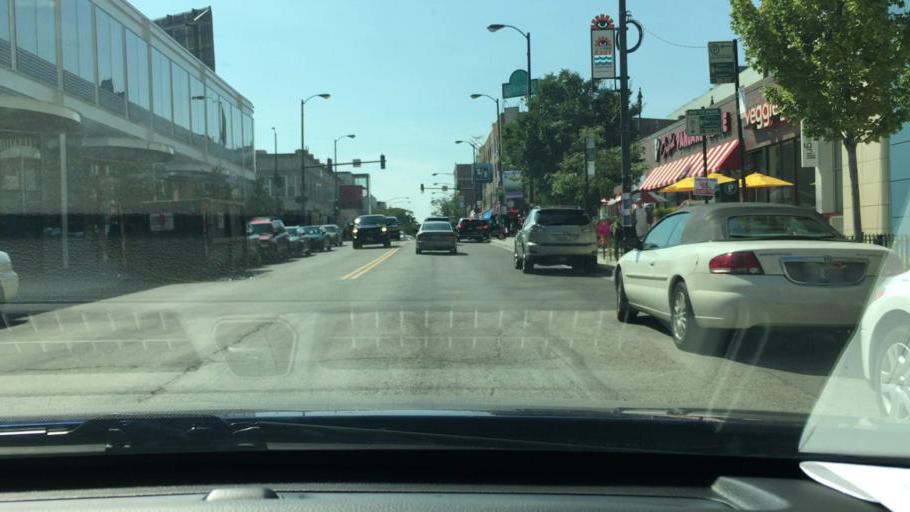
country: US
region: Illinois
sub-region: Cook County
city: Chicago
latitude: 41.9328
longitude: -87.6440
